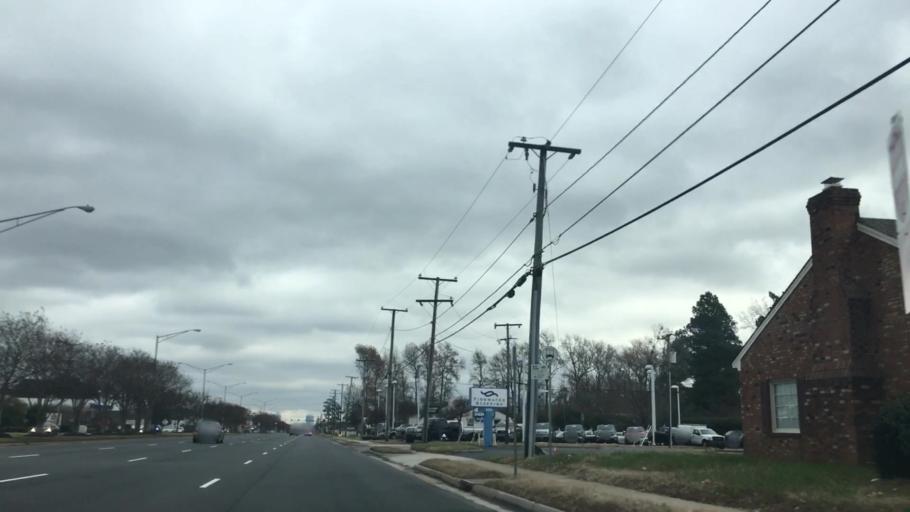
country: US
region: Virginia
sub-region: City of Chesapeake
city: Chesapeake
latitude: 36.8505
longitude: -76.1687
